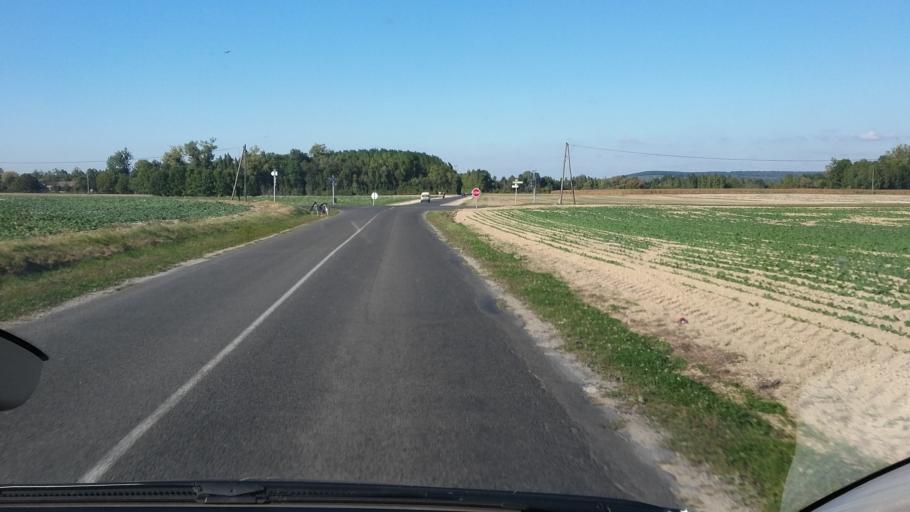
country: FR
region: Champagne-Ardenne
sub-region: Departement de la Marne
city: Connantre
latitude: 48.7848
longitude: 3.8622
